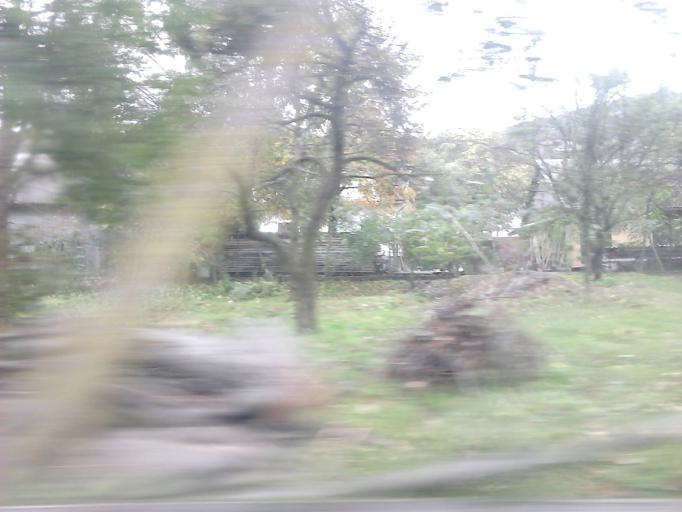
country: PL
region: Lesser Poland Voivodeship
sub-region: Powiat limanowski
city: Laskowa
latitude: 49.7187
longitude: 20.4693
